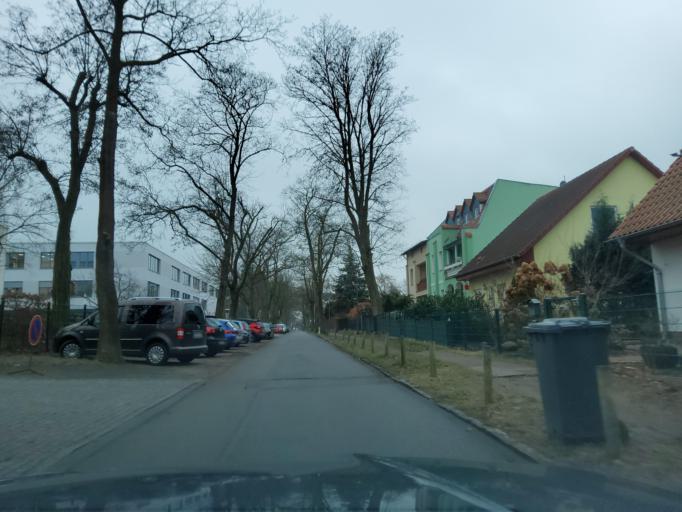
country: DE
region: Brandenburg
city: Erkner
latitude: 52.4168
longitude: 13.7529
